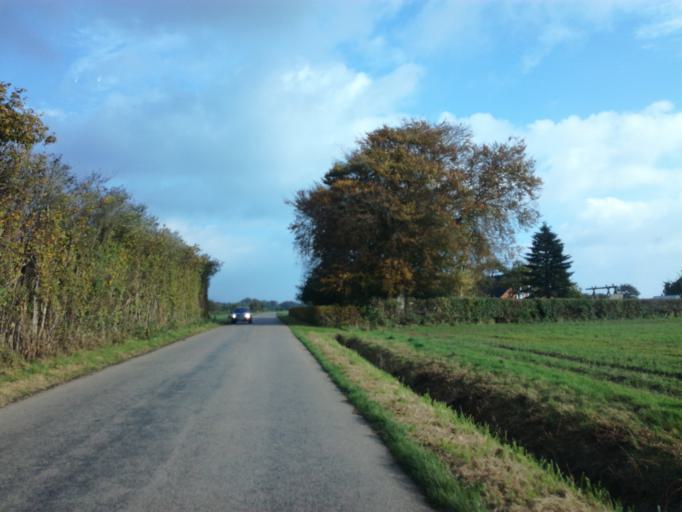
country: DK
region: South Denmark
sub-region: Vejle Kommune
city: Brejning
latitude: 55.6540
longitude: 9.6734
